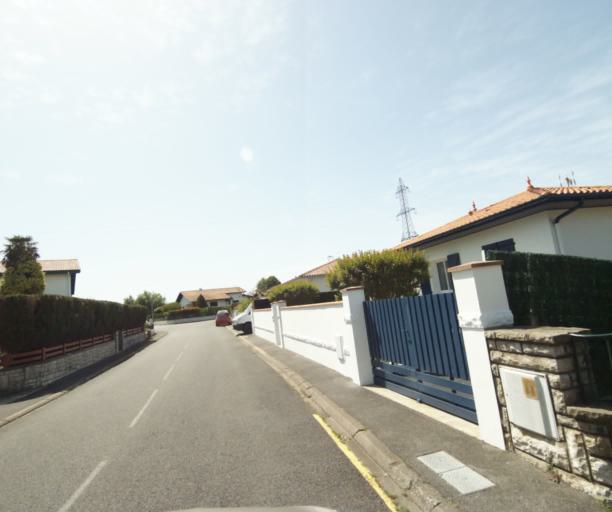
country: FR
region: Aquitaine
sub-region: Departement des Pyrenees-Atlantiques
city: Mouguerre
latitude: 43.4690
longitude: -1.4475
